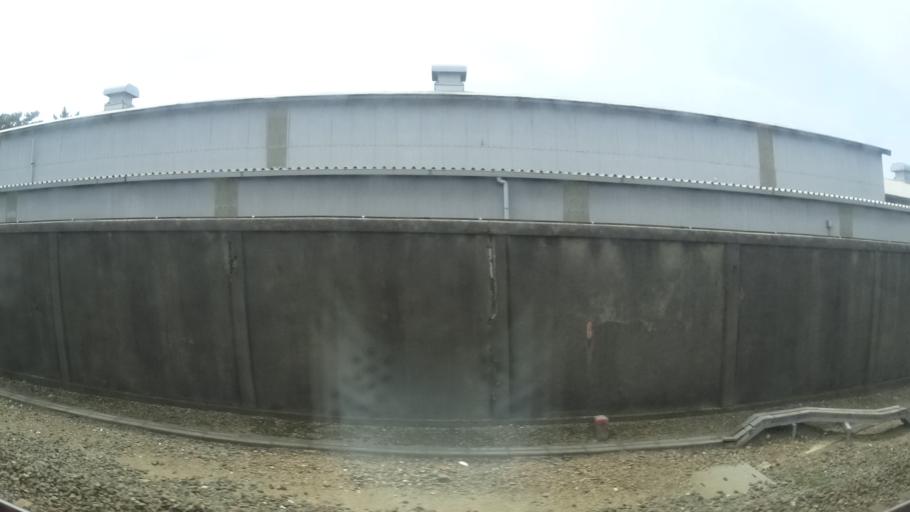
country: JP
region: Shizuoka
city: Hamamatsu
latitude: 34.6905
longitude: 137.6769
